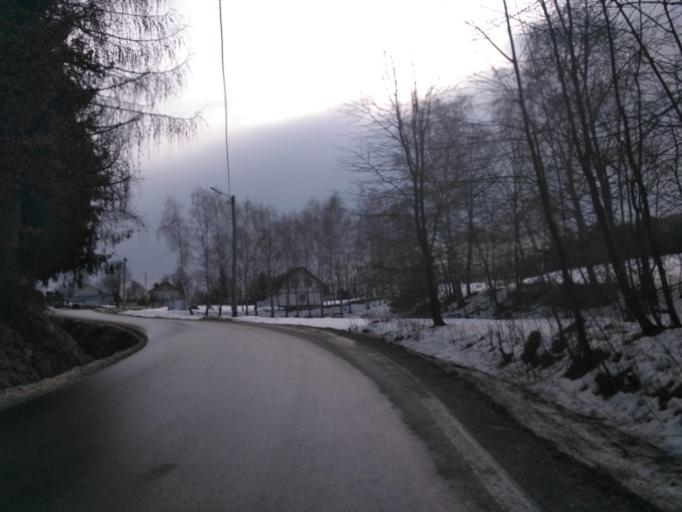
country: PL
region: Subcarpathian Voivodeship
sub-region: Powiat brzozowski
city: Dydnia
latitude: 49.6497
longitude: 22.1594
